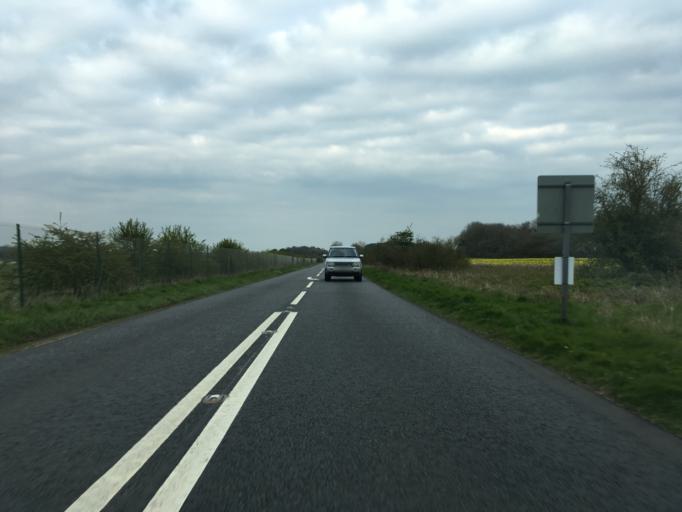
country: GB
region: England
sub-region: Gloucestershire
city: Coates
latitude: 51.6682
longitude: -2.0460
